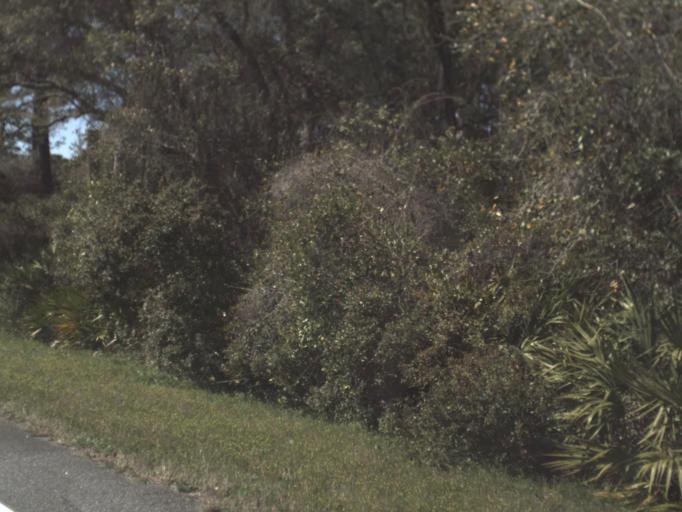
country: US
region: Florida
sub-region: Franklin County
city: Carrabelle
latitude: 29.9325
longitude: -84.4534
